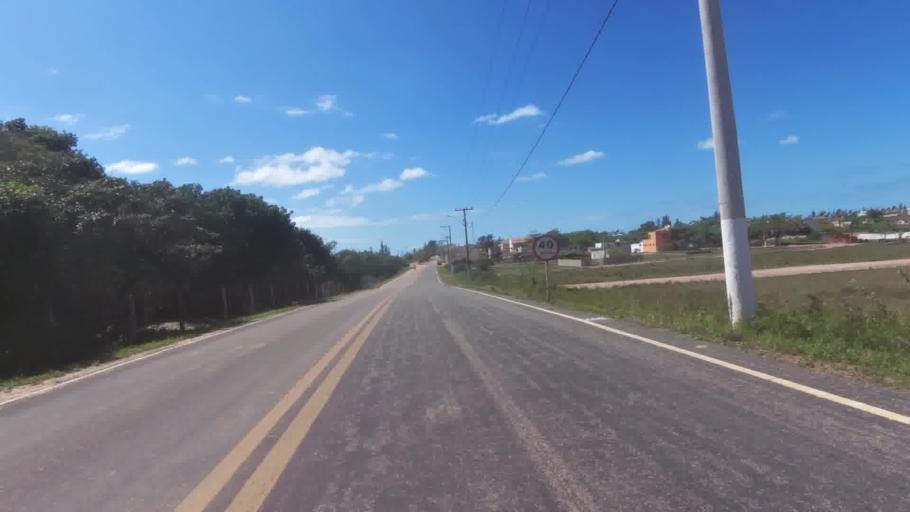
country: BR
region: Espirito Santo
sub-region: Marataizes
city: Marataizes
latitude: -21.2751
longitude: -40.9690
